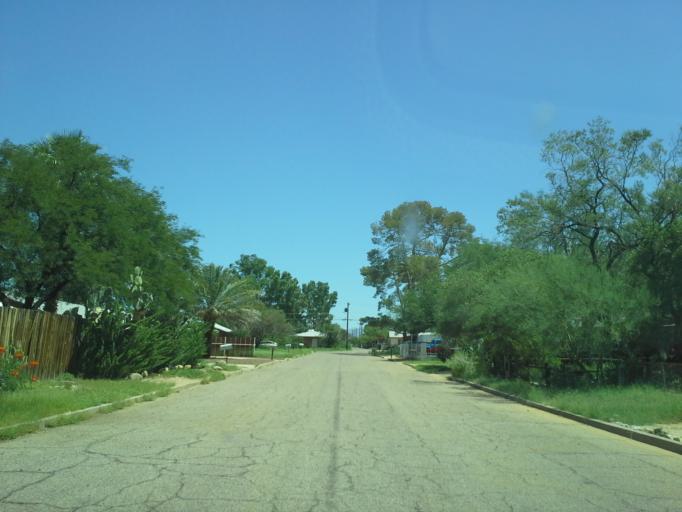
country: US
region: Arizona
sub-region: Pima County
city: Tucson
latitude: 32.2550
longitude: -110.9345
